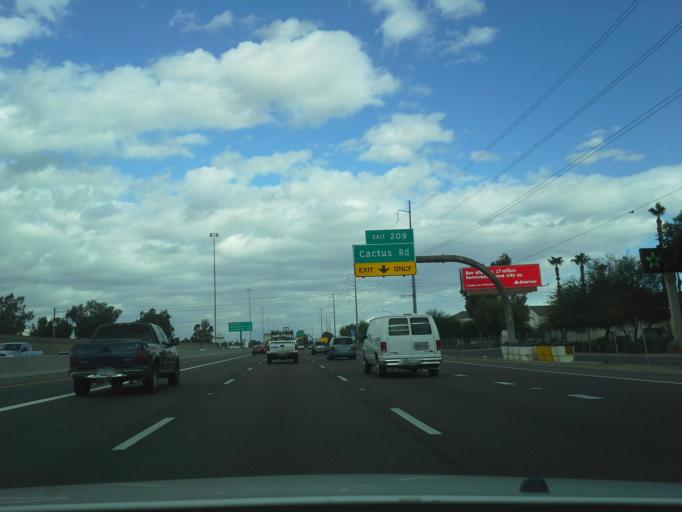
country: US
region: Arizona
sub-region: Maricopa County
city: Glendale
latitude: 33.5877
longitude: -112.1168
